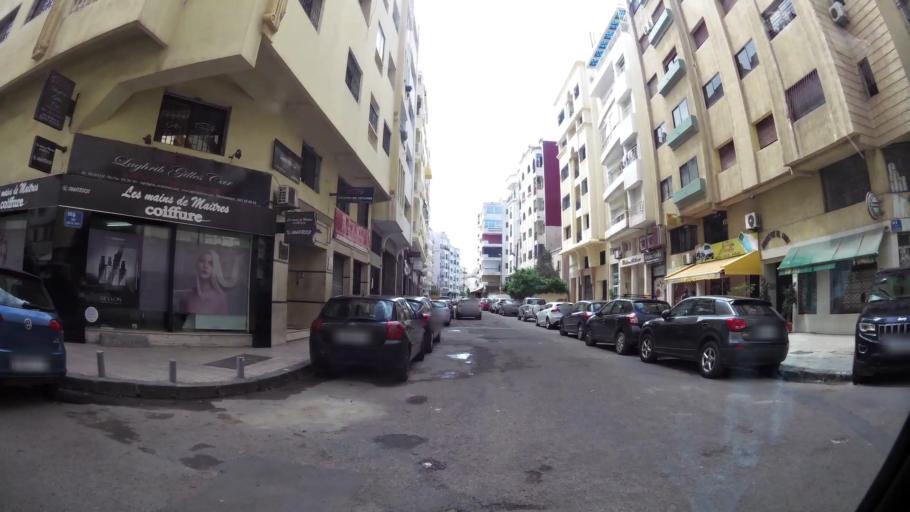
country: MA
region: Grand Casablanca
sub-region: Casablanca
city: Casablanca
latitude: 33.5955
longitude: -7.6403
